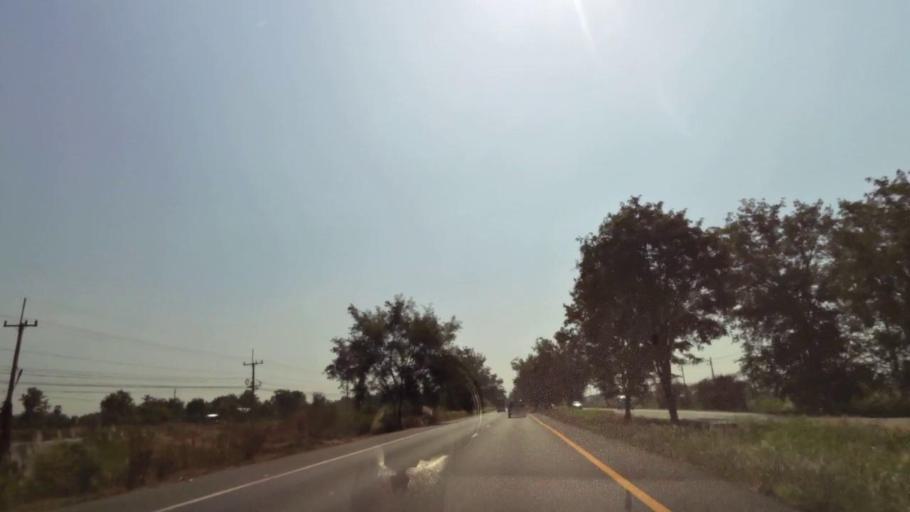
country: TH
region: Nakhon Sawan
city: Kao Liao
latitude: 15.9404
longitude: 100.1137
